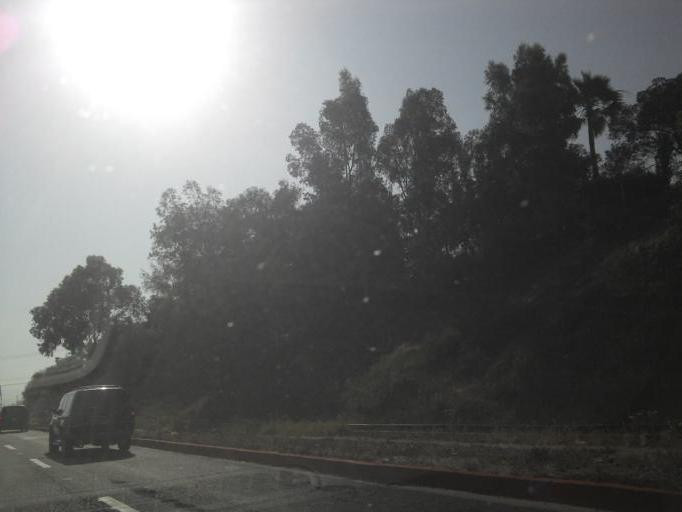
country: MX
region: Baja California
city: Tijuana
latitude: 32.5107
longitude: -116.9900
